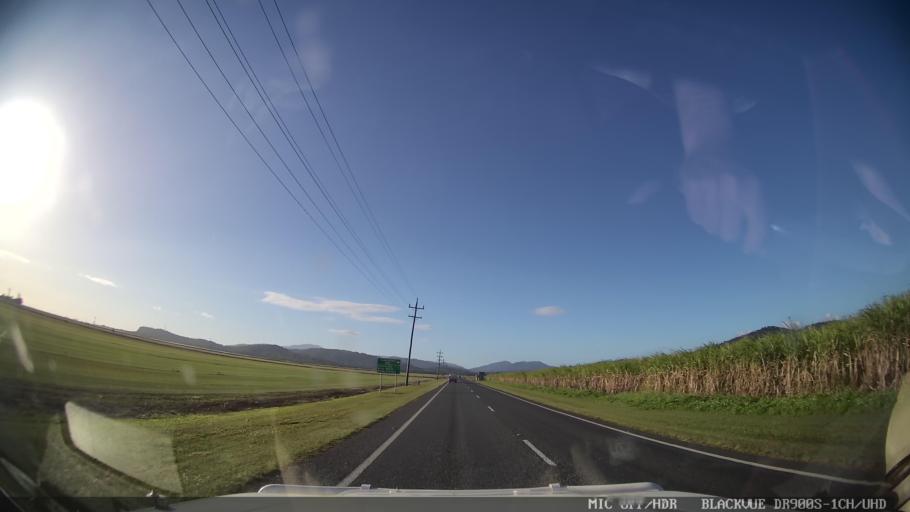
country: AU
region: Queensland
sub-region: Whitsunday
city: Proserpine
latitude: -20.3896
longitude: 148.5865
